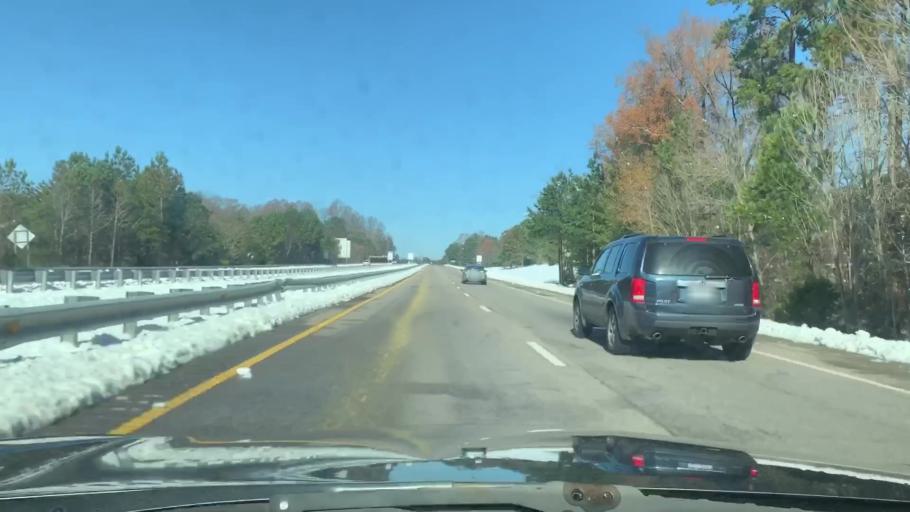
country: US
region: North Carolina
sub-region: Durham County
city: Durham
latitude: 36.0235
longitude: -78.9588
